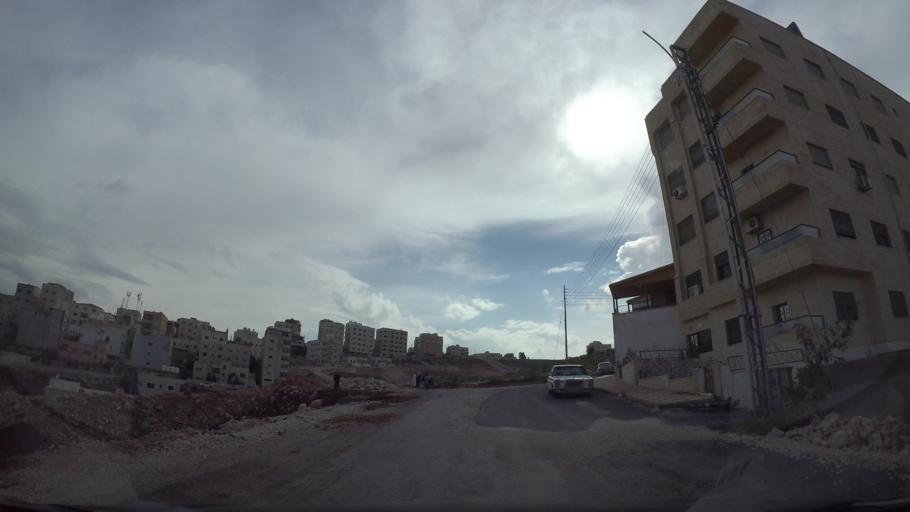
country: JO
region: Amman
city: Amman
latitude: 32.0158
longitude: 35.9432
